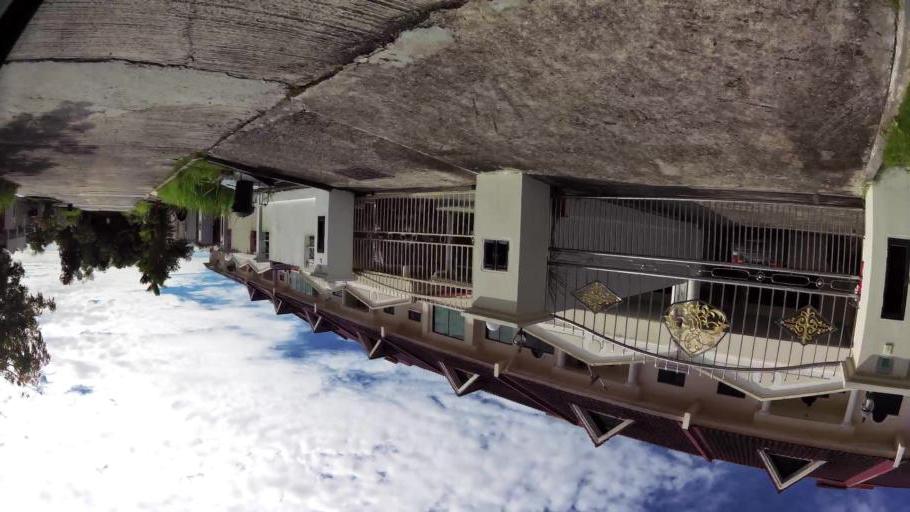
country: BN
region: Brunei and Muara
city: Bandar Seri Begawan
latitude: 4.9044
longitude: 114.9746
